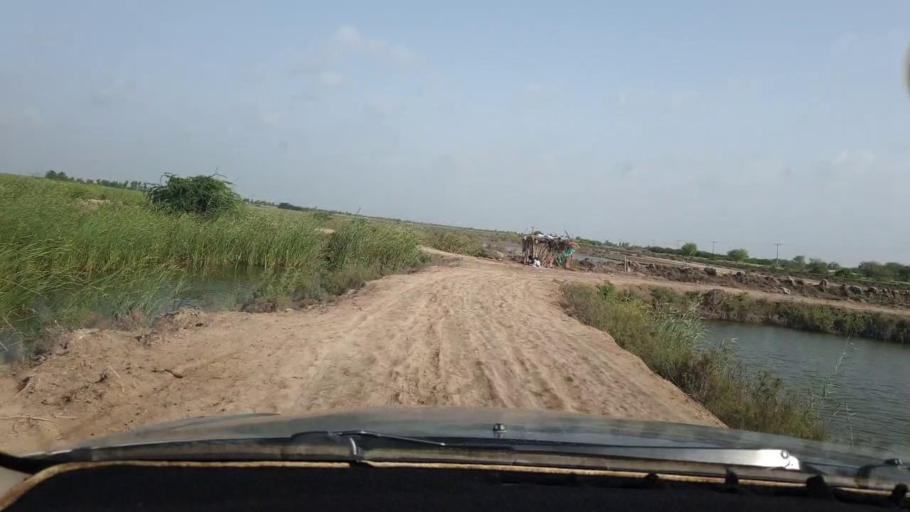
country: PK
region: Sindh
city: Tando Bago
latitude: 24.8160
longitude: 68.9363
